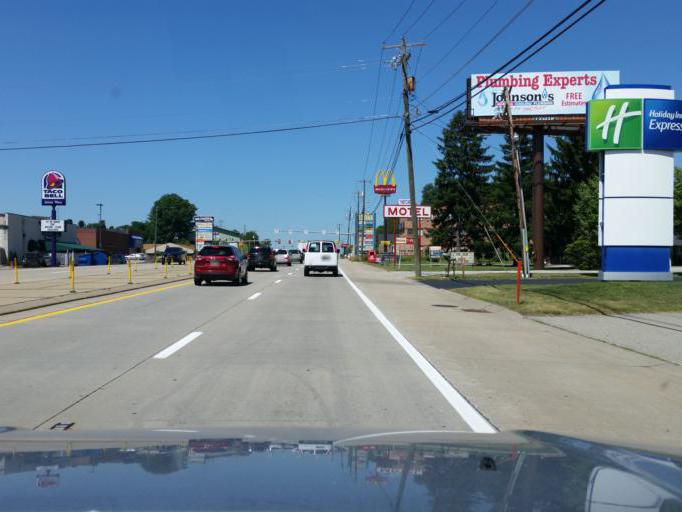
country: US
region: Pennsylvania
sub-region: Westmoreland County
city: Delmont
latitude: 40.4000
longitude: -79.5828
